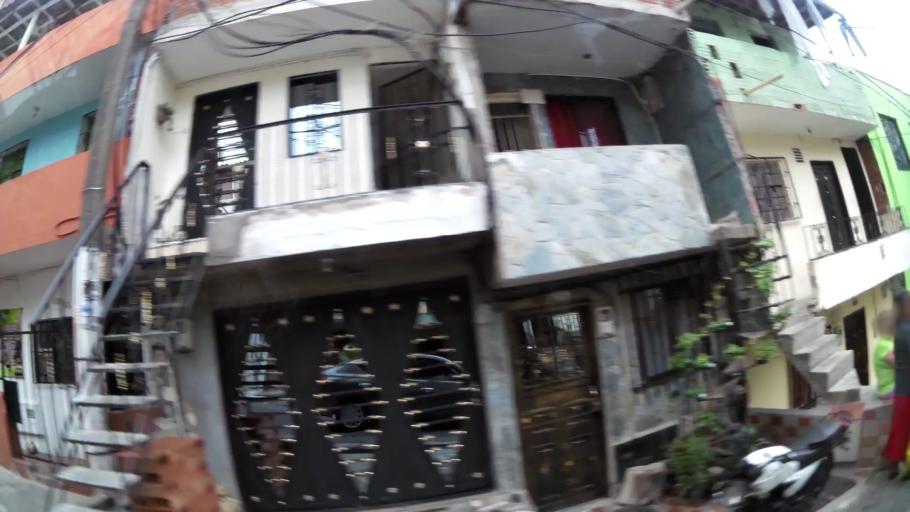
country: CO
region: Antioquia
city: Bello
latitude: 6.3051
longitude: -75.5543
